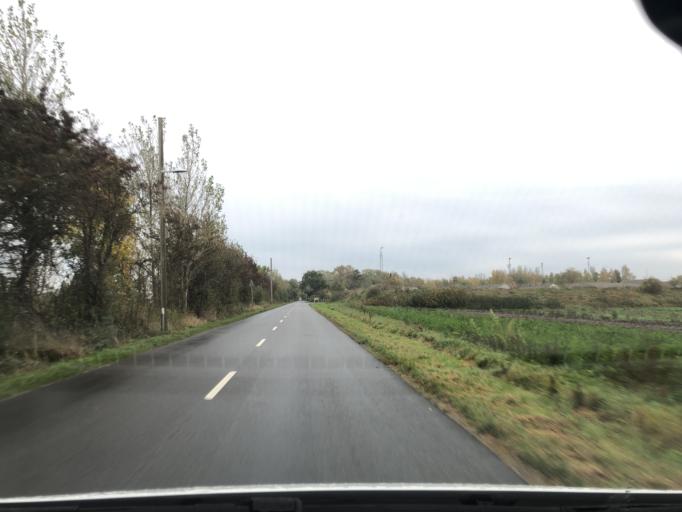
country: DK
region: Capital Region
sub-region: Tarnby Kommune
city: Tarnby
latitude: 55.5671
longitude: 12.5846
